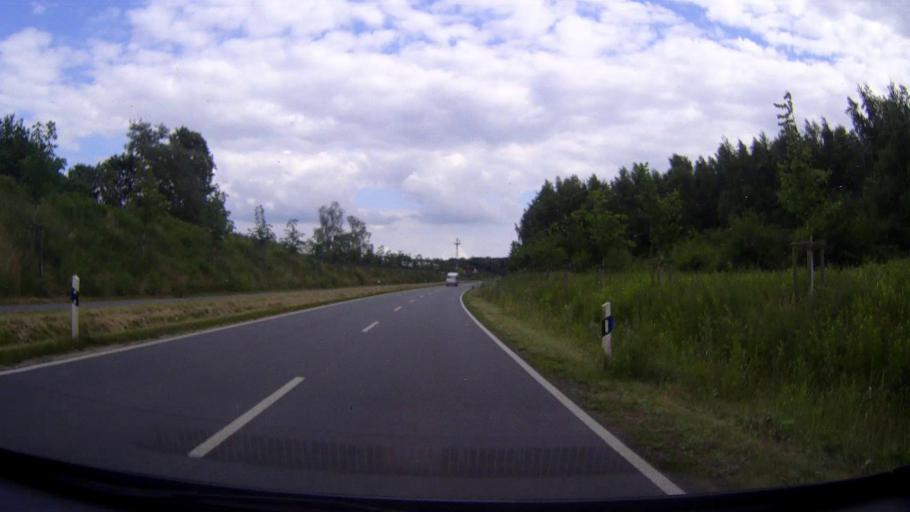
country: DE
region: Schleswig-Holstein
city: Stockelsdorf
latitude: 53.8721
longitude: 10.6099
